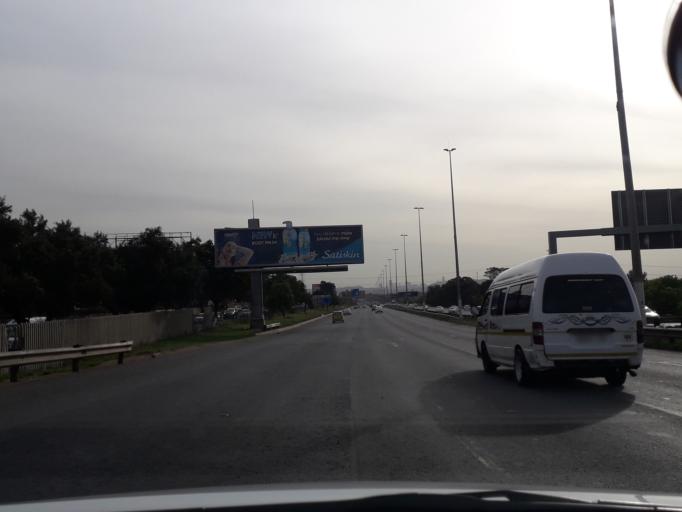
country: ZA
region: Gauteng
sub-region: City of Johannesburg Metropolitan Municipality
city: Modderfontein
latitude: -26.1424
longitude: 28.1888
